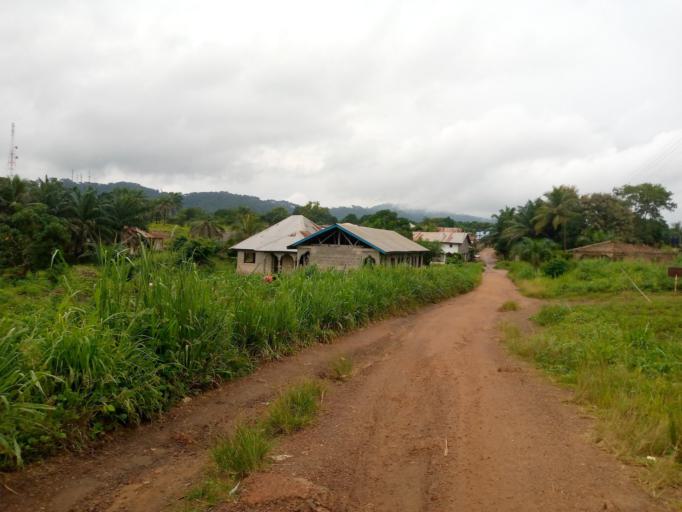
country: SL
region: Eastern Province
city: Kenema
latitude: 7.8440
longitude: -11.2026
